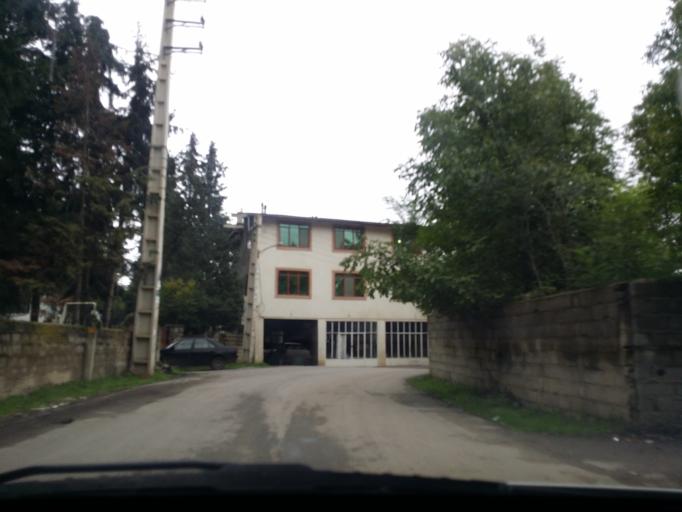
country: IR
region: Mazandaran
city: `Abbasabad
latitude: 36.5067
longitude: 51.1900
